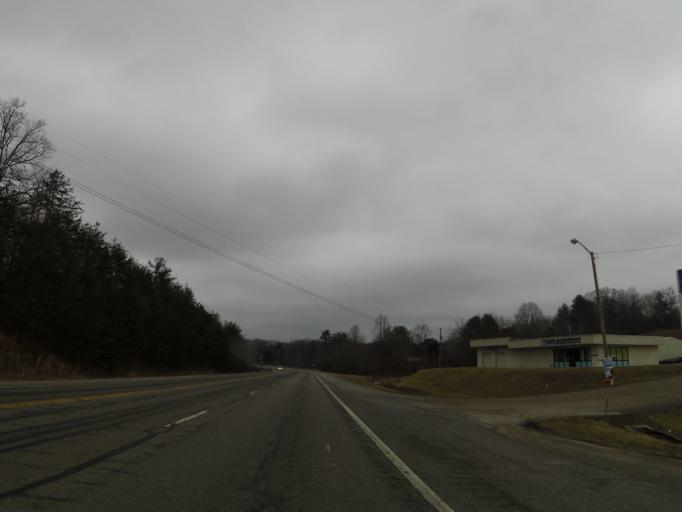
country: US
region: Tennessee
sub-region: Scott County
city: Huntsville
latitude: 36.3986
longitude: -84.5400
